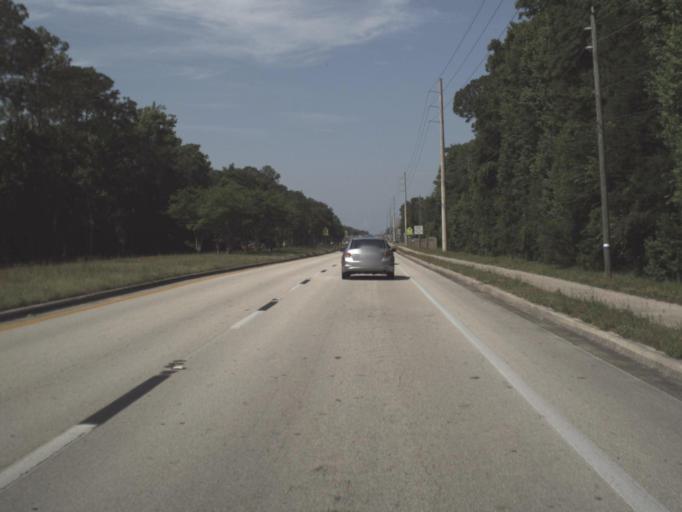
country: US
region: Florida
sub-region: Saint Johns County
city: Saint Augustine South
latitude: 29.8348
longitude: -81.3715
